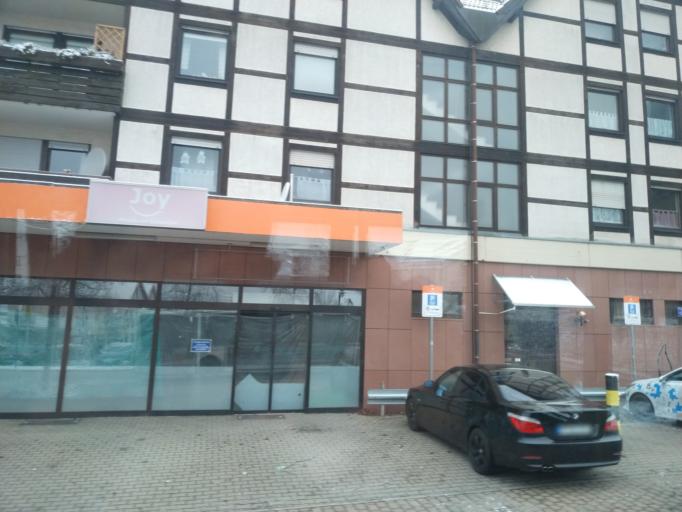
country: DE
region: Baden-Wuerttemberg
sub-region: Karlsruhe Region
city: Birkenfeld
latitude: 48.8710
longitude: 8.6376
